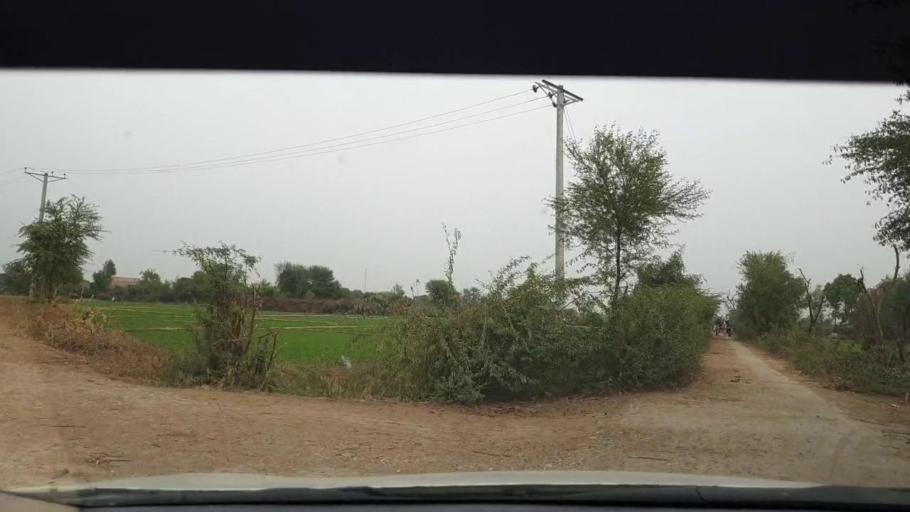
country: PK
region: Sindh
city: Berani
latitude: 25.8948
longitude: 68.7724
